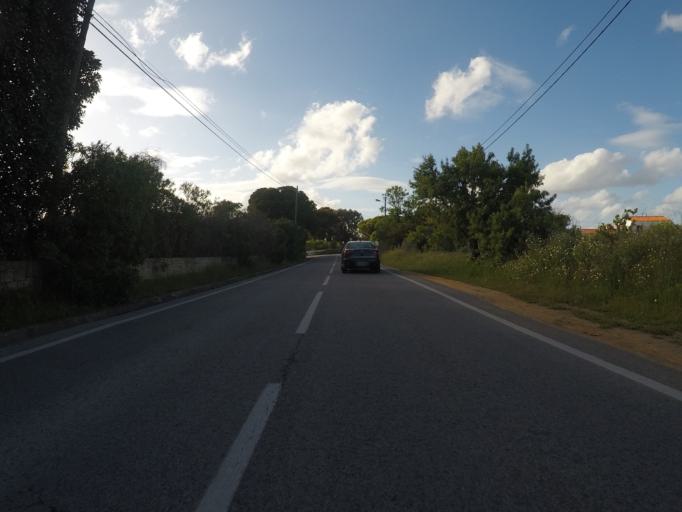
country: PT
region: Faro
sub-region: Lagoa
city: Carvoeiro
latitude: 37.1000
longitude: -8.4431
